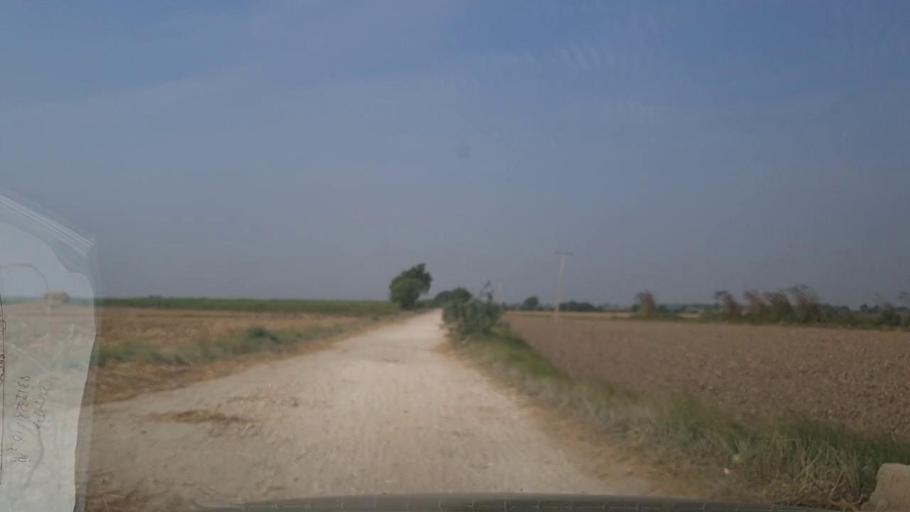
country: PK
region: Sindh
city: Bulri
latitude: 24.9710
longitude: 68.3105
